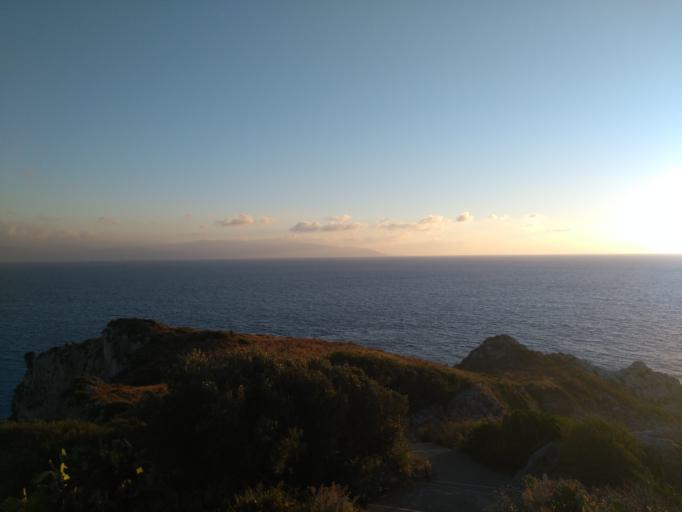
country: IT
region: Sicily
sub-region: Messina
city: Milazzo
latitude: 38.2696
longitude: 15.2273
